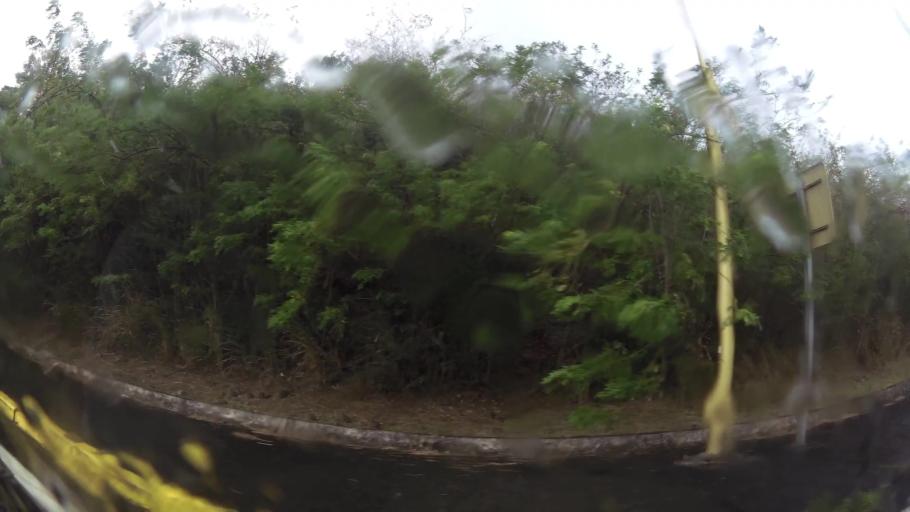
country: MQ
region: Martinique
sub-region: Martinique
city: Sainte-Luce
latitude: 14.4720
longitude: -60.9530
